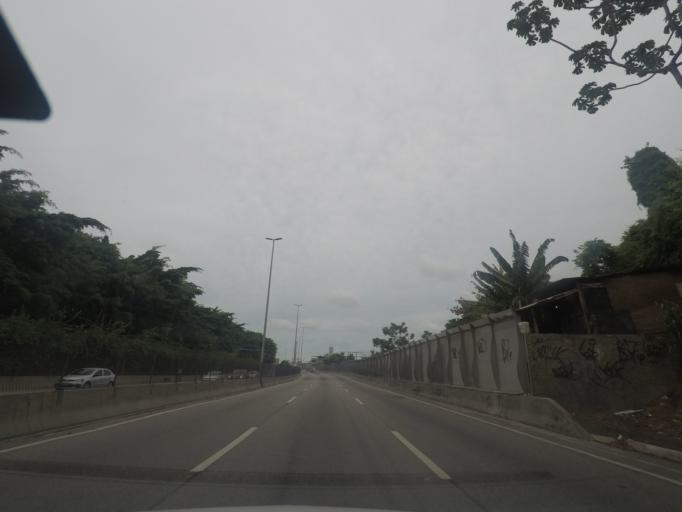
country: BR
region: Rio de Janeiro
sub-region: Sao Joao De Meriti
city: Sao Joao de Meriti
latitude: -22.9482
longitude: -43.3557
